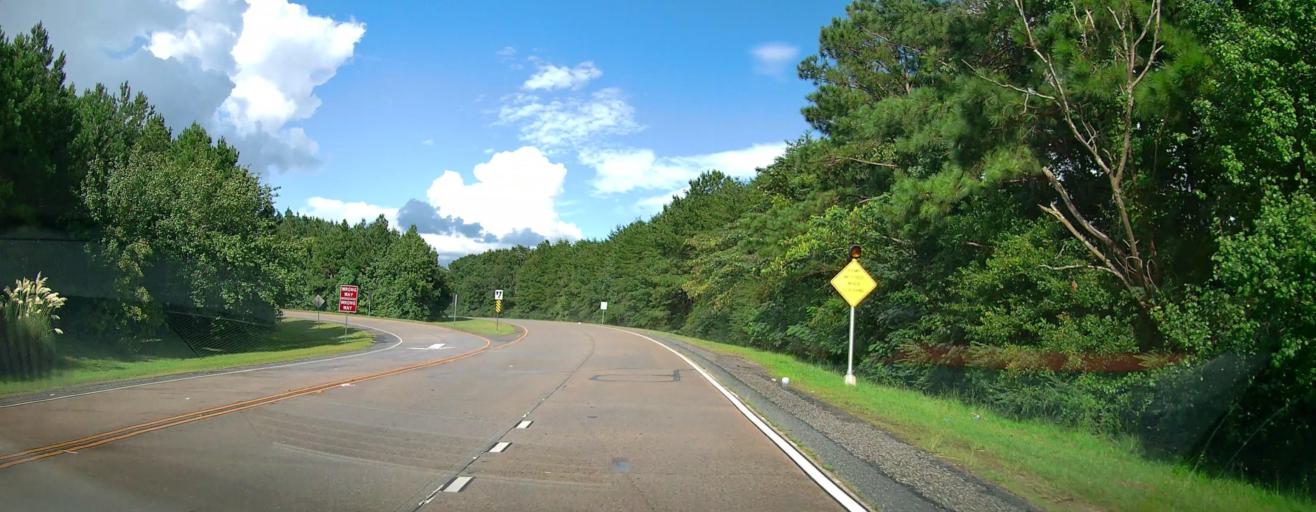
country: US
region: Alabama
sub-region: Russell County
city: Phenix City
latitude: 32.5210
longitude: -84.9877
